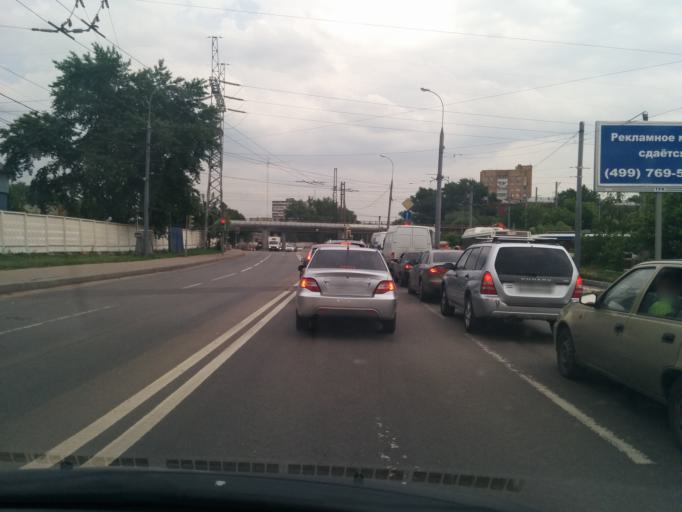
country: RU
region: Moscow
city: Likhobory
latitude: 55.8440
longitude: 37.5586
